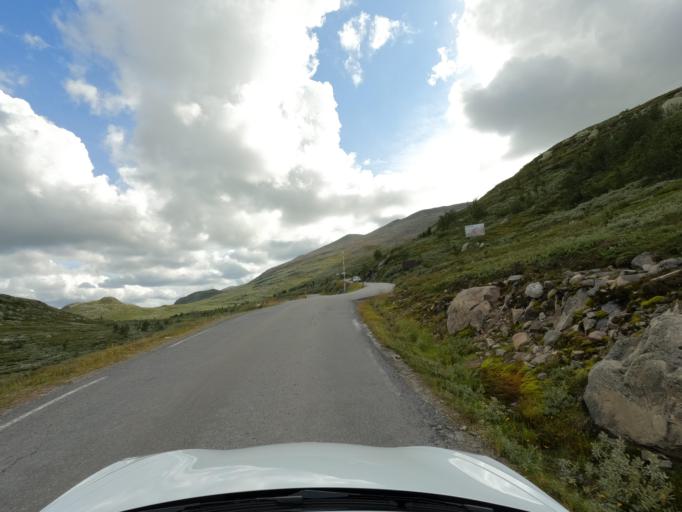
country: NO
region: Telemark
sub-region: Tinn
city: Rjukan
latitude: 59.8581
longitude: 8.6867
